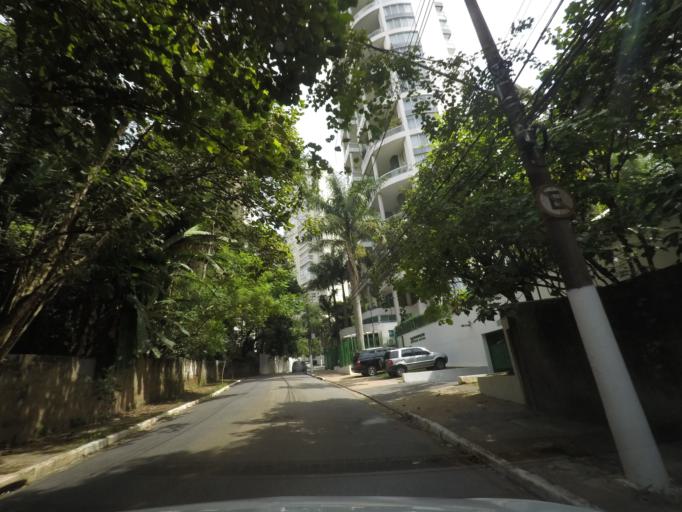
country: BR
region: Sao Paulo
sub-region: Taboao Da Serra
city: Taboao da Serra
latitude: -23.6276
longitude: -46.7206
